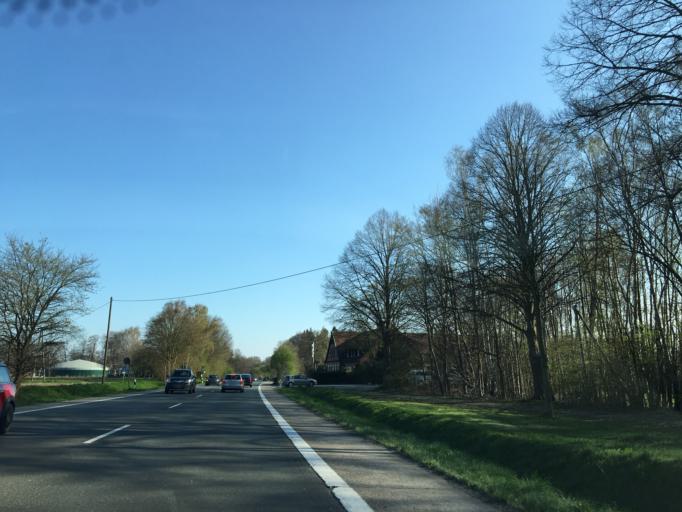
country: DE
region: North Rhine-Westphalia
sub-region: Regierungsbezirk Munster
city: Greven
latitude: 52.0743
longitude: 7.6601
